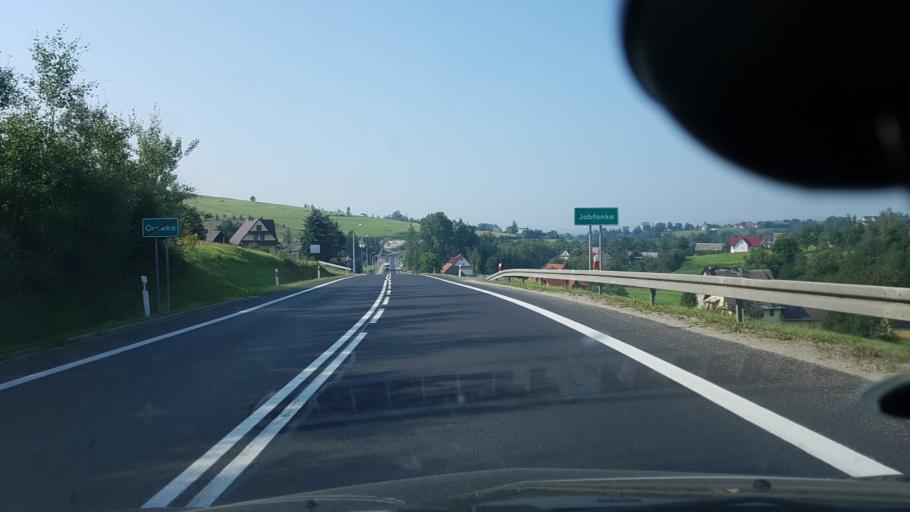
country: PL
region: Lesser Poland Voivodeship
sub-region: Powiat nowotarski
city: Jablonka
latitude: 49.5022
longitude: 19.7121
